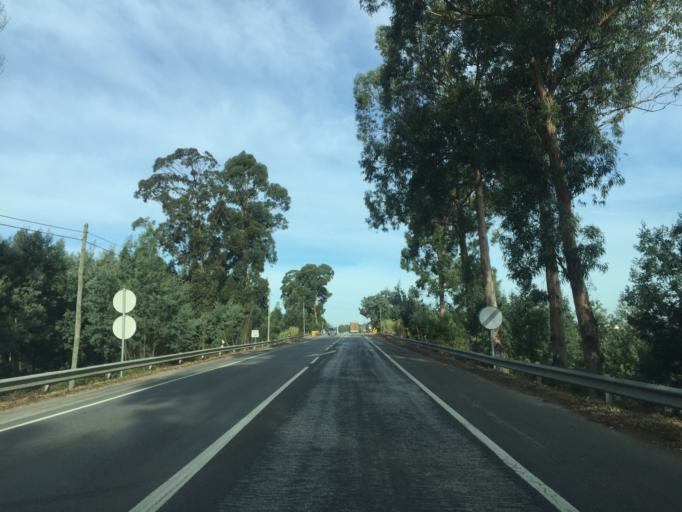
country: PT
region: Coimbra
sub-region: Figueira da Foz
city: Lavos
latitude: 40.0204
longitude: -8.8158
